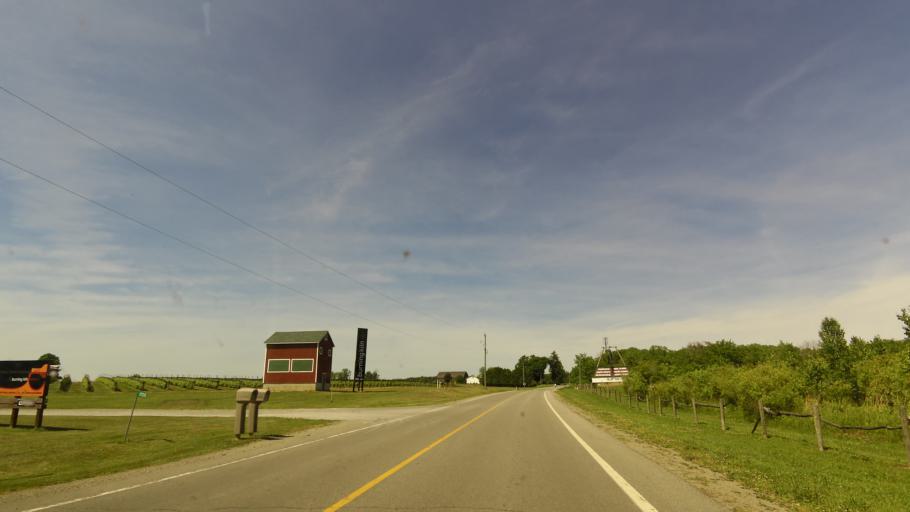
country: CA
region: Ontario
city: Norfolk County
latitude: 42.6891
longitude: -80.3507
